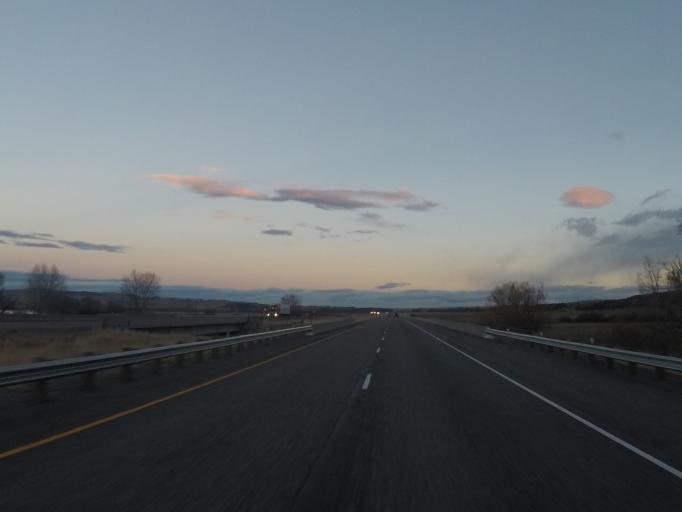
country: US
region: Montana
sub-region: Sweet Grass County
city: Big Timber
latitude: 45.7935
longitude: -109.8339
